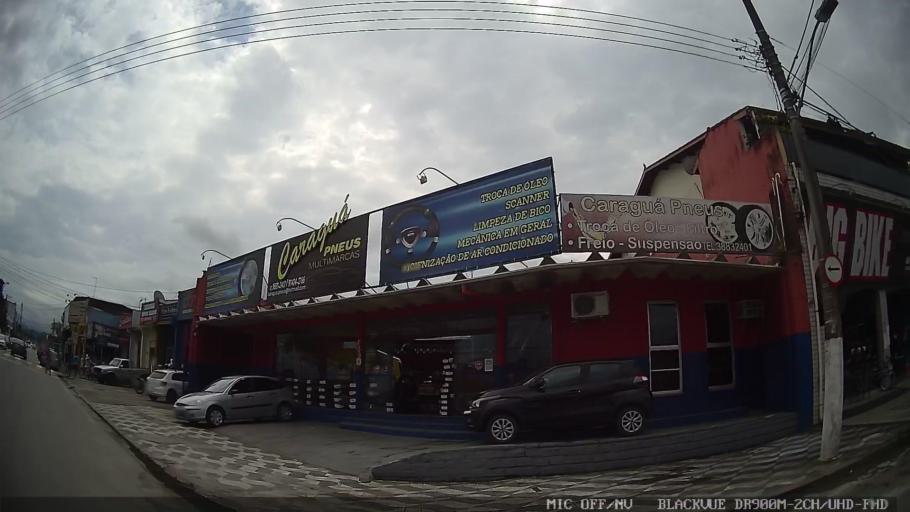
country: BR
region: Sao Paulo
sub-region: Caraguatatuba
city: Caraguatatuba
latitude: -23.6246
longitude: -45.4177
